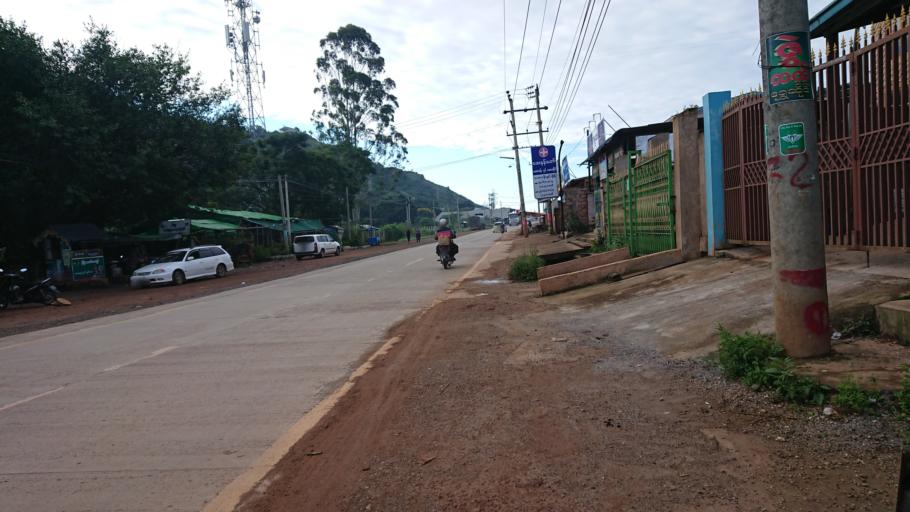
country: MM
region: Shan
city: Taunggyi
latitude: 20.7475
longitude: 97.0501
